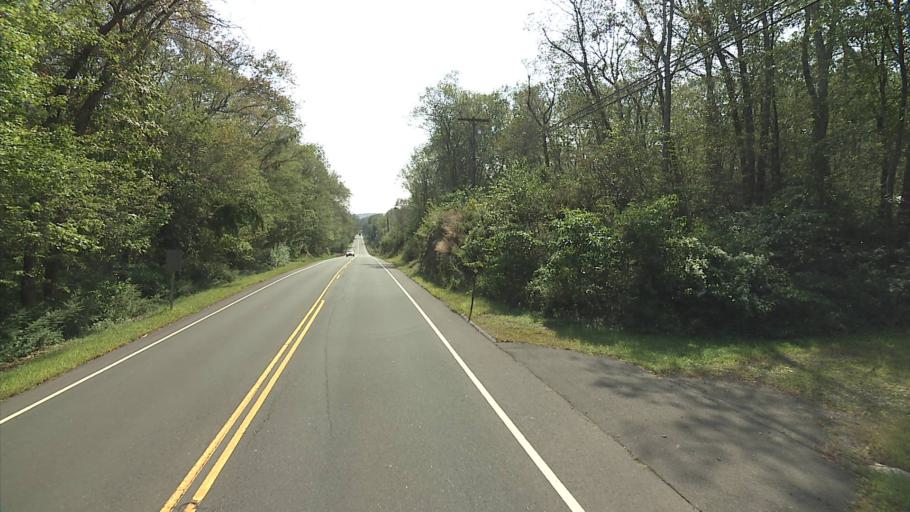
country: US
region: Connecticut
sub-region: Middlesex County
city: Durham
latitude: 41.4431
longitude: -72.6606
